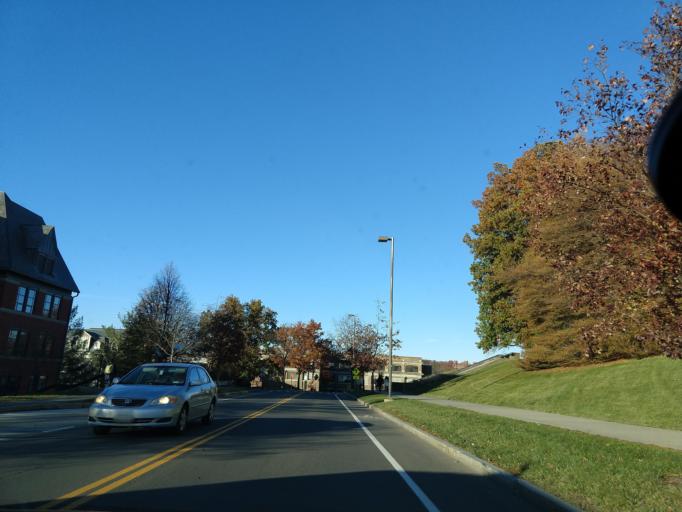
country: US
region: New York
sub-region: Tompkins County
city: East Ithaca
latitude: 42.4499
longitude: -76.4828
